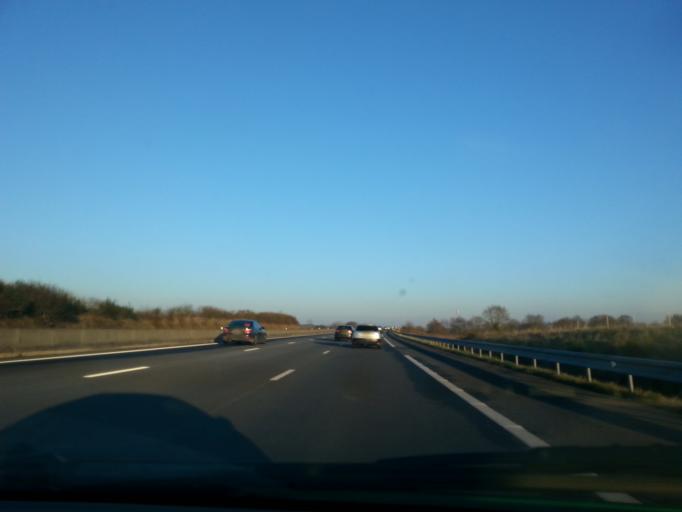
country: FR
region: Pays de la Loire
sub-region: Departement de la Sarthe
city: Tuffe
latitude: 48.1069
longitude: 0.5532
